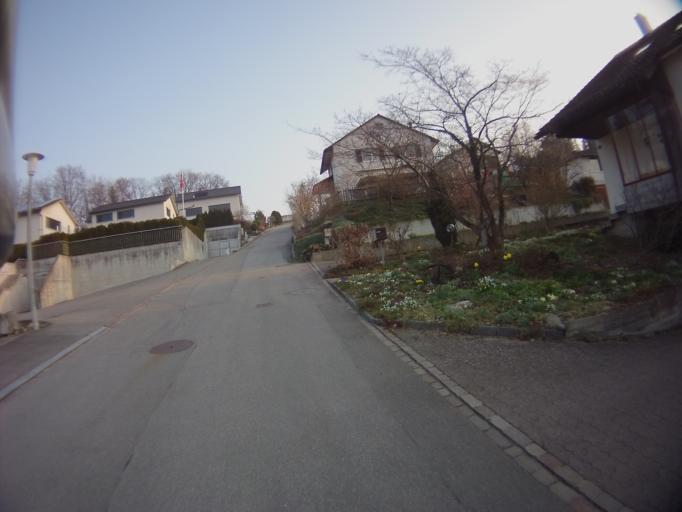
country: CH
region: Zurich
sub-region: Bezirk Affoltern
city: Obfelden / Toussen
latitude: 47.2669
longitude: 8.4285
